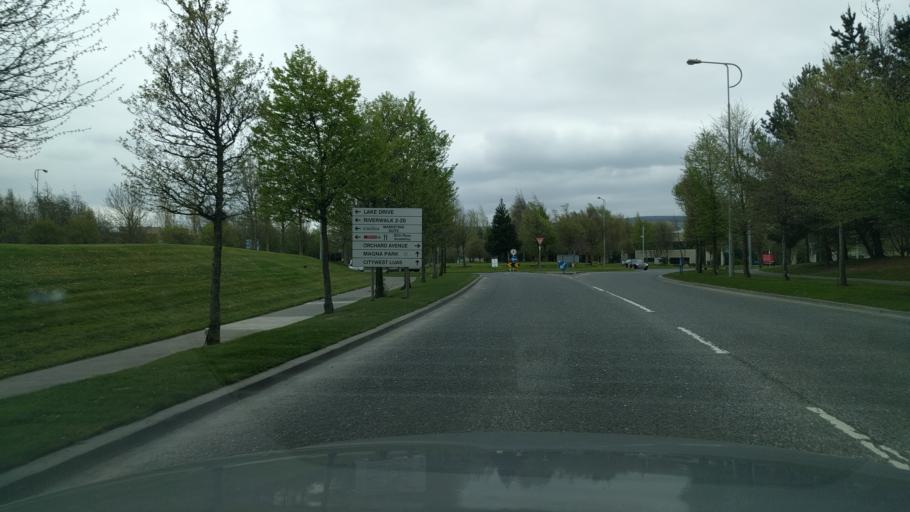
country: IE
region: Leinster
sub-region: South Dublin
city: Saggart
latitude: 53.2902
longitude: -6.4267
